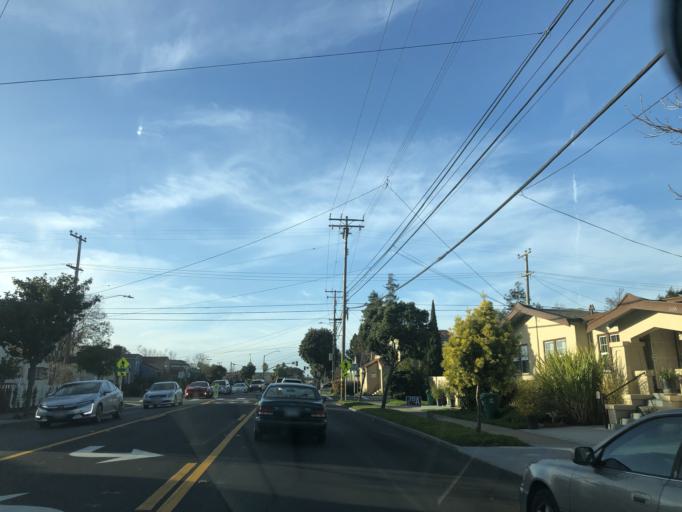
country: US
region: California
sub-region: Alameda County
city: Alameda
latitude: 37.7566
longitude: -122.2468
